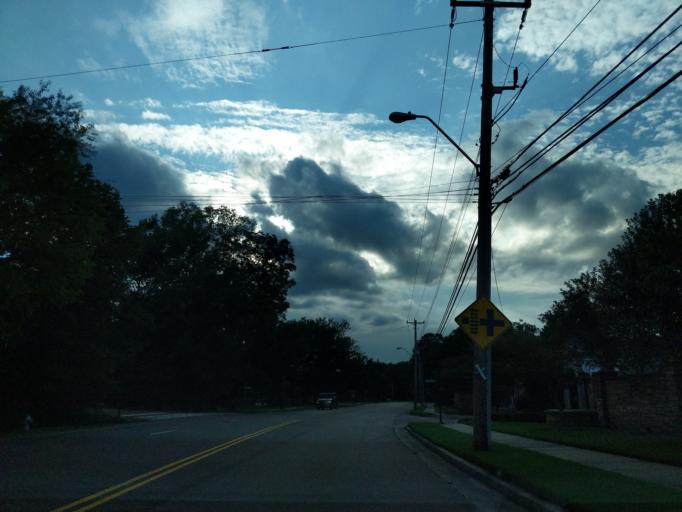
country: US
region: Tennessee
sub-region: Shelby County
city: Germantown
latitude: 35.0631
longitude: -89.7624
